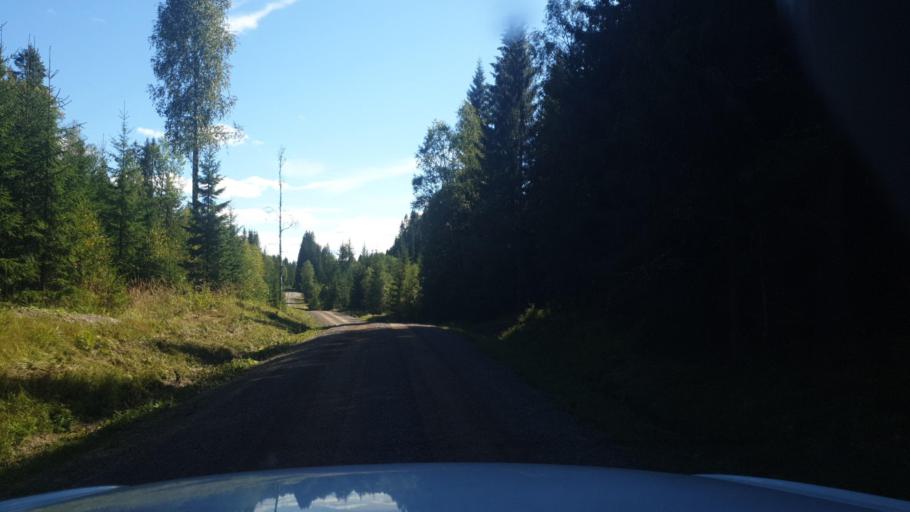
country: SE
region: Vaermland
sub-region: Eda Kommun
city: Charlottenberg
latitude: 60.0404
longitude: 12.5816
